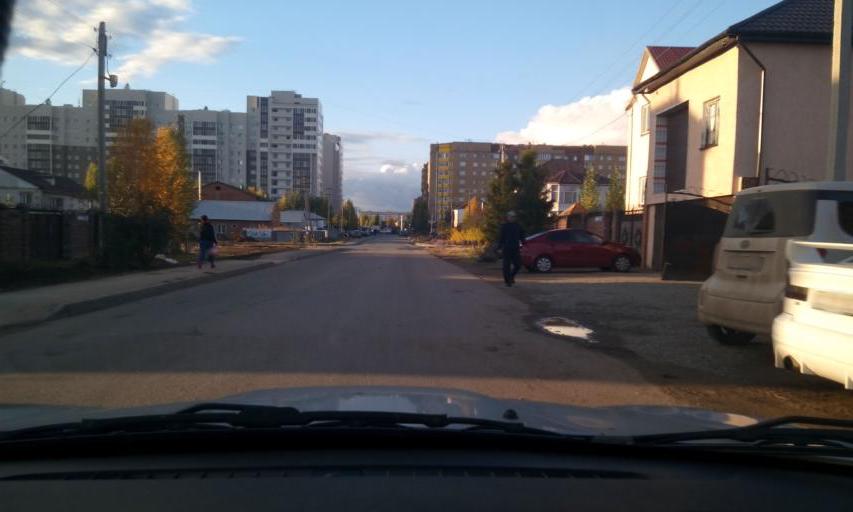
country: KZ
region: Astana Qalasy
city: Astana
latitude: 51.1385
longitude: 71.4869
